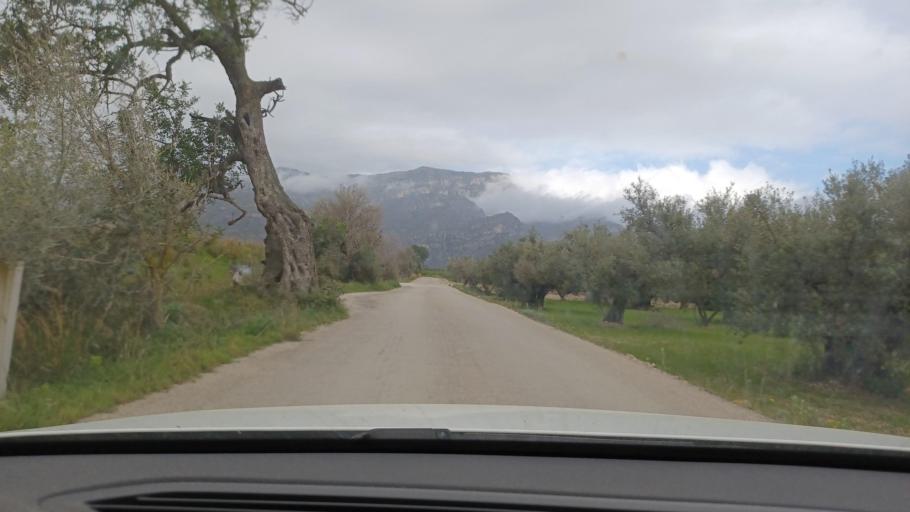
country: ES
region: Catalonia
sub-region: Provincia de Tarragona
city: Tortosa
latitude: 40.7967
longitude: 0.4321
